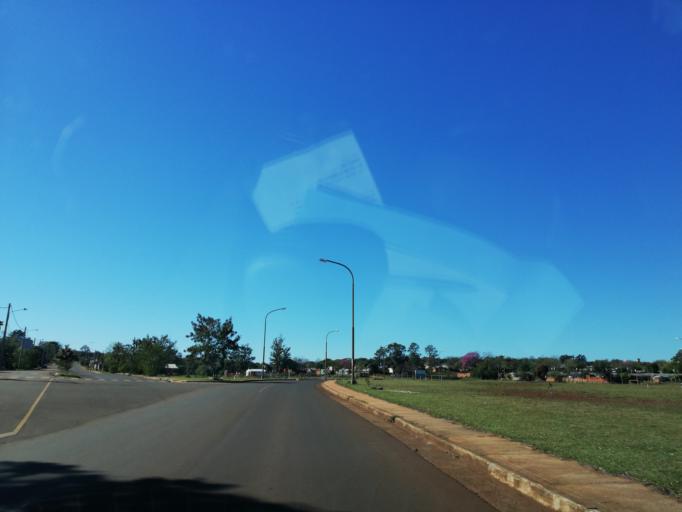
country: AR
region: Misiones
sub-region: Departamento de Capital
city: Posadas
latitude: -27.3855
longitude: -55.9506
